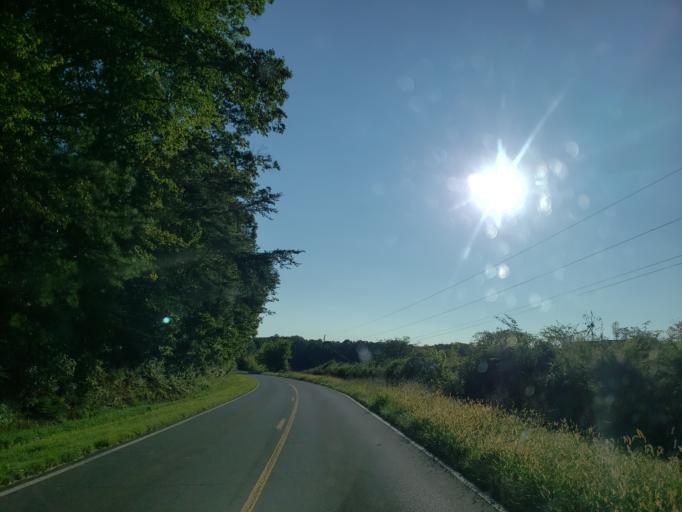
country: US
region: Georgia
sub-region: Bartow County
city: Rydal
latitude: 34.2909
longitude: -84.7926
